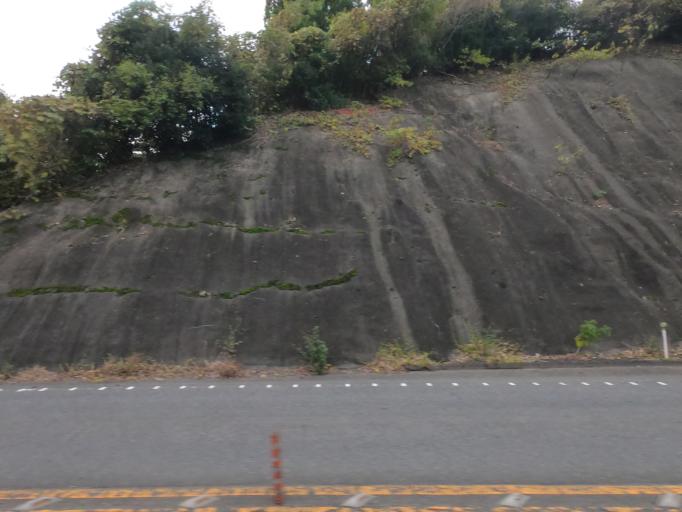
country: JP
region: Kumamoto
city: Minamata
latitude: 32.2515
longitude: 130.5029
